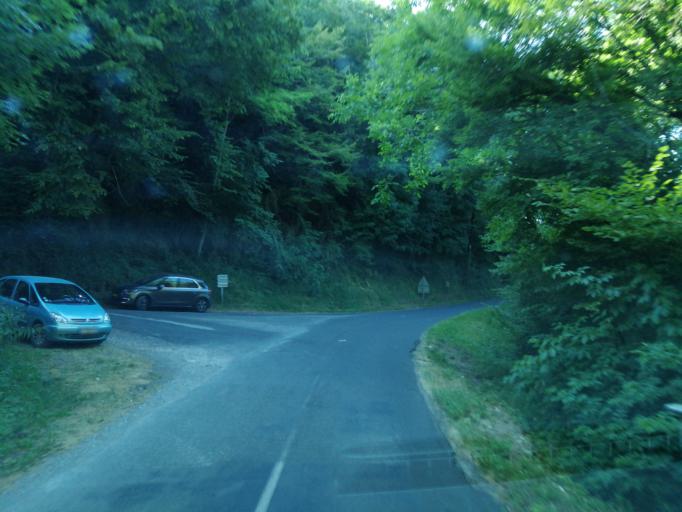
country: FR
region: Midi-Pyrenees
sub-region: Departement du Lot
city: Souillac
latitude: 44.8721
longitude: 1.4110
